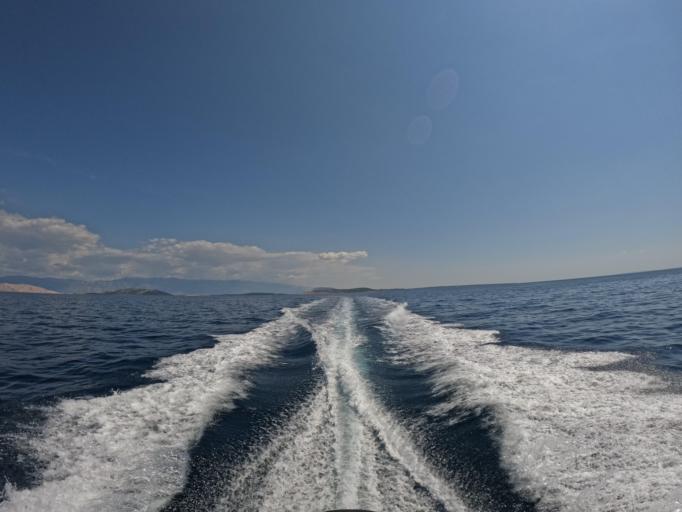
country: HR
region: Primorsko-Goranska
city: Lopar
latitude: 44.8867
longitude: 14.6403
